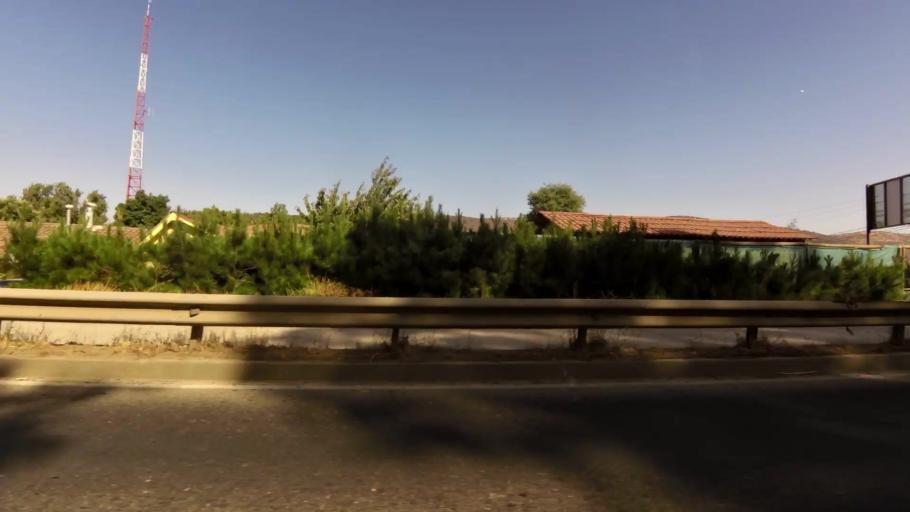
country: CL
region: Maule
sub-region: Provincia de Talca
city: Talca
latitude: -35.4165
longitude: -71.6740
